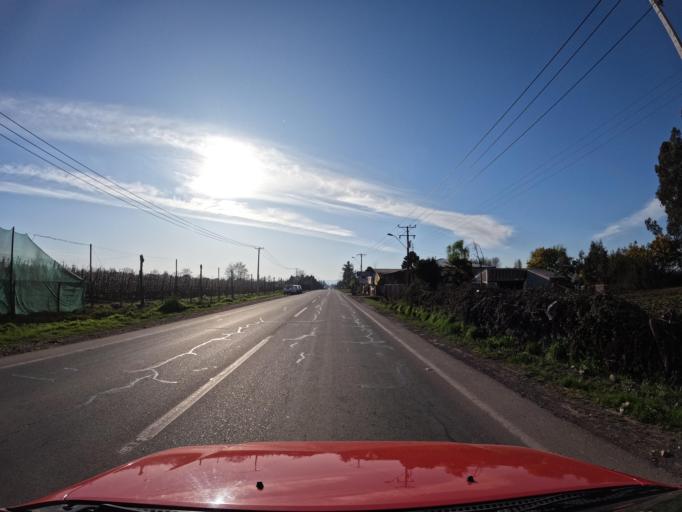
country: CL
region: Maule
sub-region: Provincia de Curico
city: Teno
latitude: -34.8928
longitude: -71.0659
